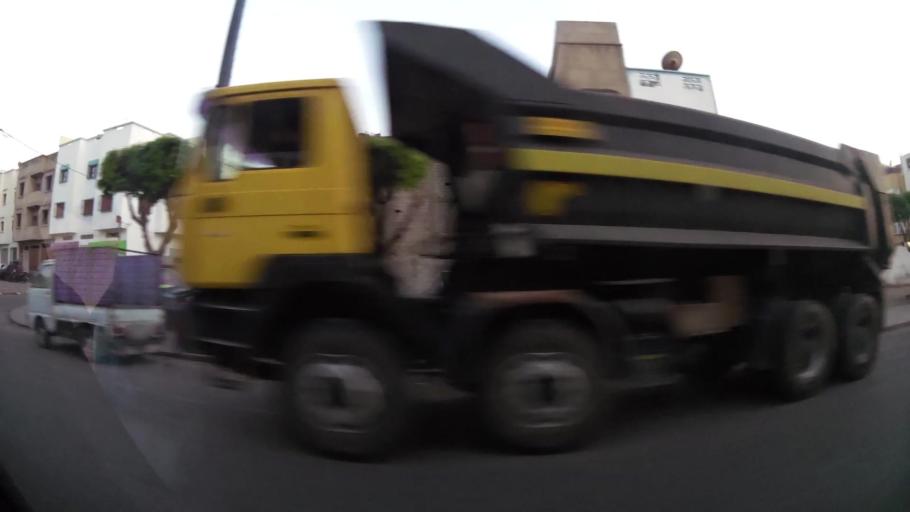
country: MA
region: Souss-Massa-Draa
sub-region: Inezgane-Ait Mellou
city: Inezgane
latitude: 30.3783
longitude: -9.5004
